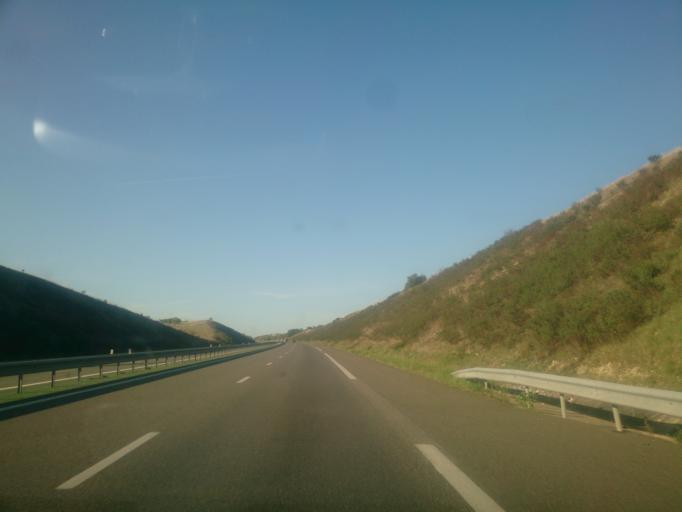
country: FR
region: Midi-Pyrenees
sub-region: Departement du Lot
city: Cahors
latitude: 44.5210
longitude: 1.5094
